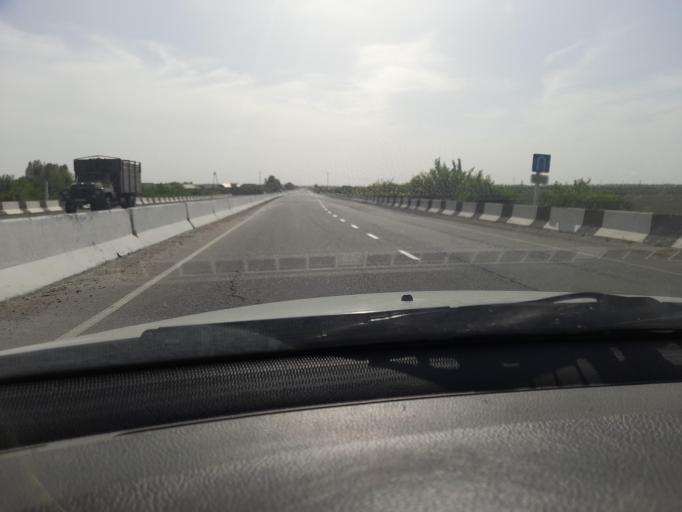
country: UZ
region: Samarqand
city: Kattaqo'rg'on
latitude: 39.9220
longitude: 66.3522
